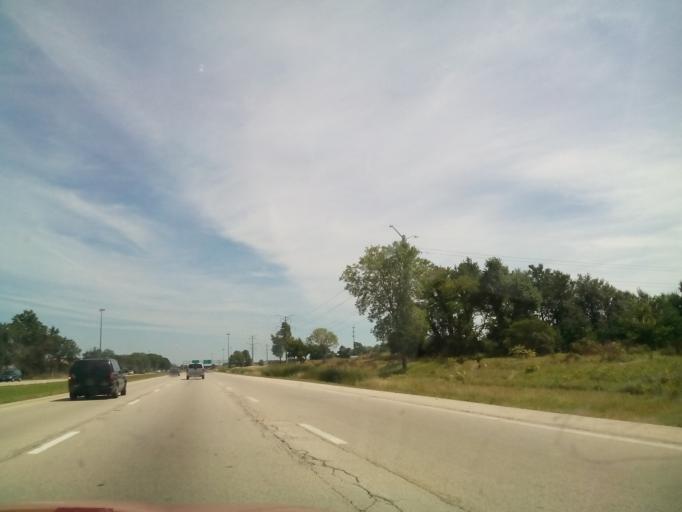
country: US
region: Illinois
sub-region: Winnebago County
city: Cherry Valley
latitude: 42.2199
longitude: -89.0249
